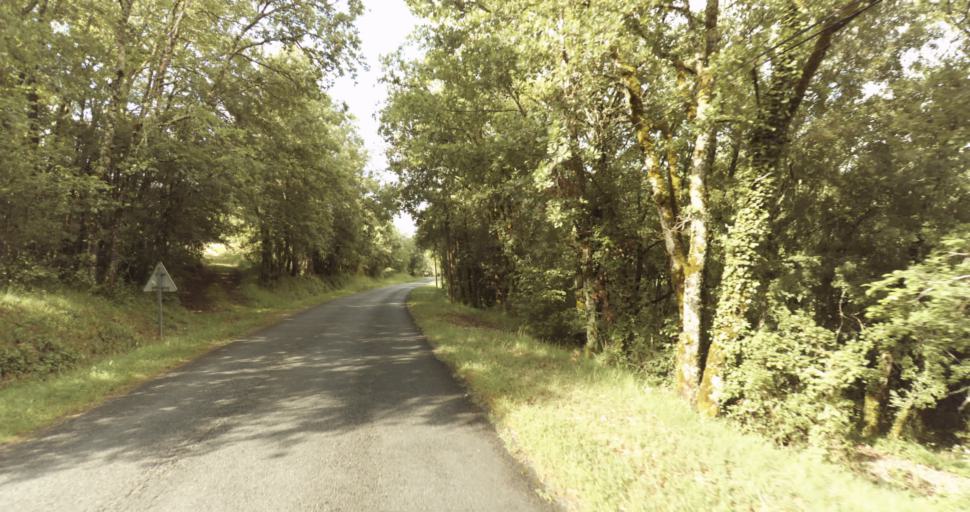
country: FR
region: Aquitaine
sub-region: Departement de la Dordogne
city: Lalinde
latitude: 44.9171
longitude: 0.8094
